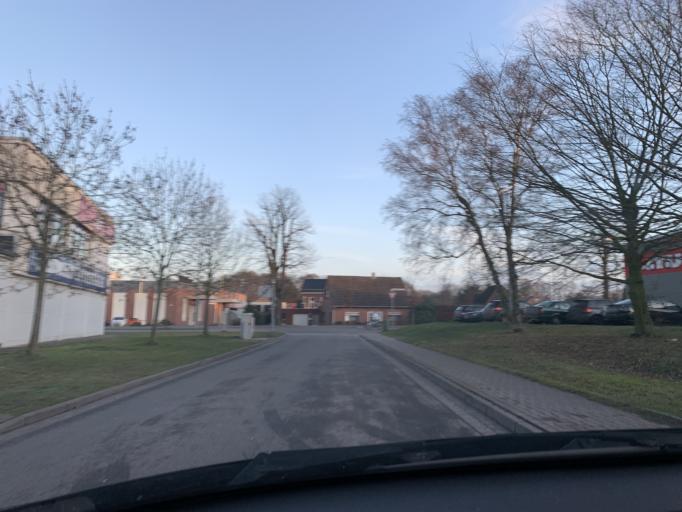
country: DE
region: Lower Saxony
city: Oldenburg
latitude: 53.1727
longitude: 8.2290
